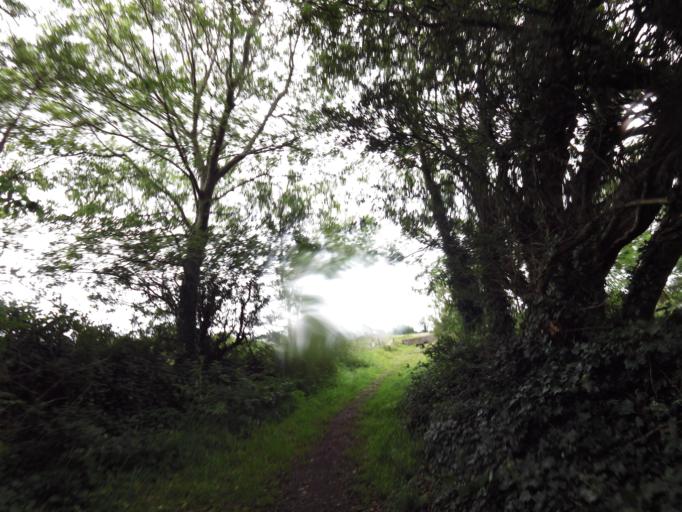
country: IE
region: Connaught
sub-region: County Galway
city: Athenry
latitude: 53.2861
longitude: -8.7119
